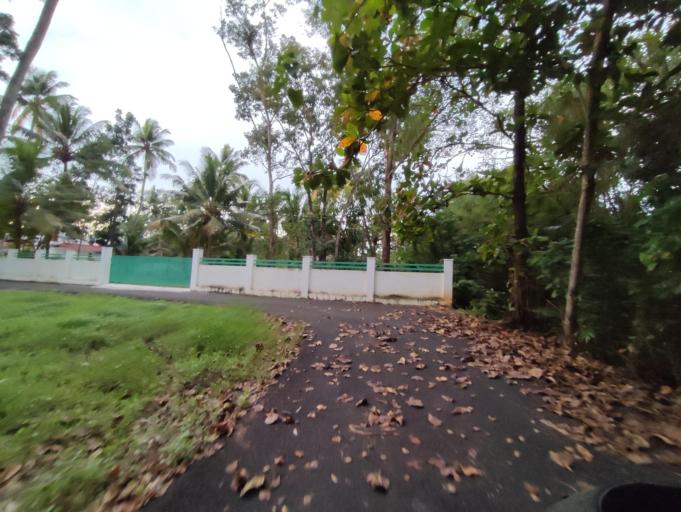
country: IN
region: Kerala
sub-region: Alappuzha
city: Vayalar
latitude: 9.6969
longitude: 76.3359
